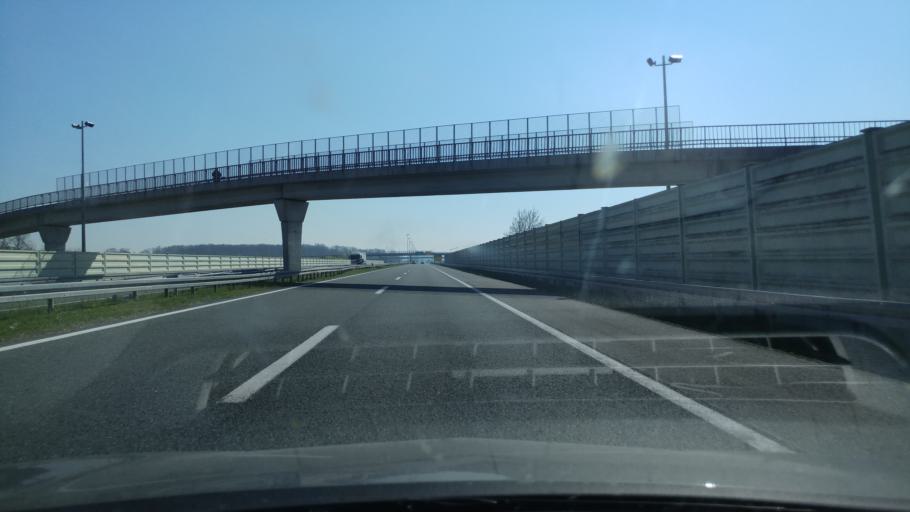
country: HR
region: Brodsko-Posavska
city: Bukovlje
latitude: 45.1796
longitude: 18.0588
